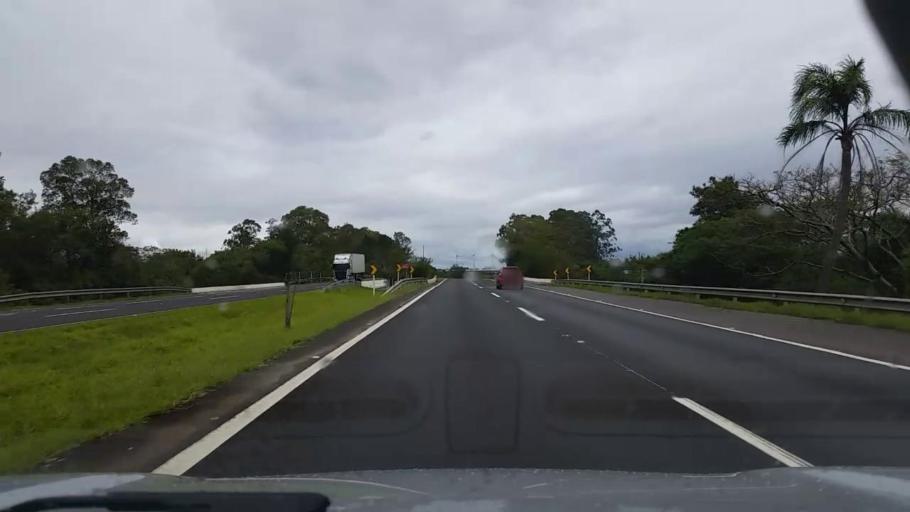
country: BR
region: Rio Grande do Sul
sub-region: Osorio
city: Osorio
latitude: -29.8908
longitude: -50.2805
